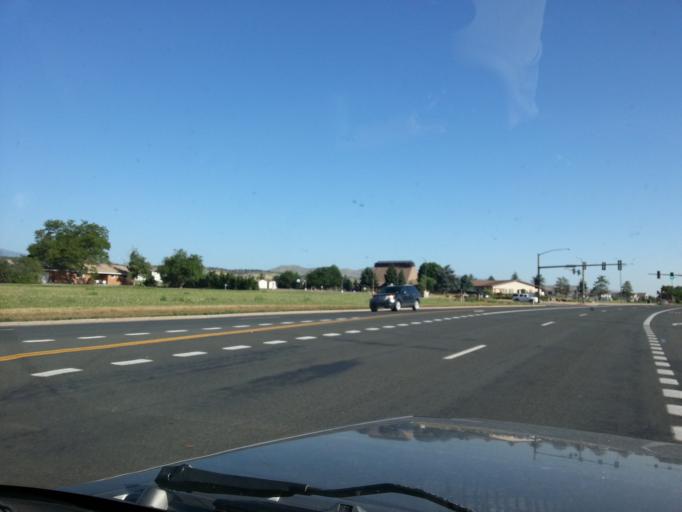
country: US
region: Colorado
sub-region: Larimer County
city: Loveland
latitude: 40.4209
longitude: -105.1154
